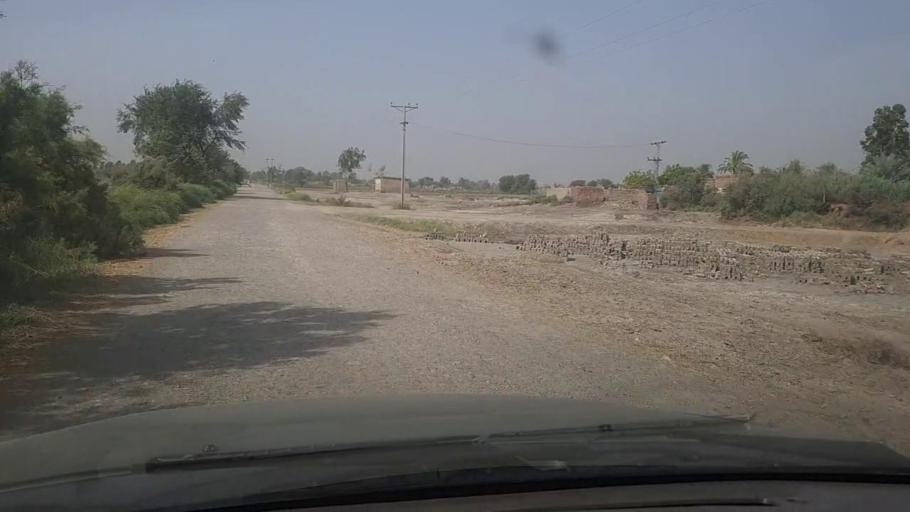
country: PK
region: Sindh
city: Garhi Yasin
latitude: 27.8770
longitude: 68.5645
